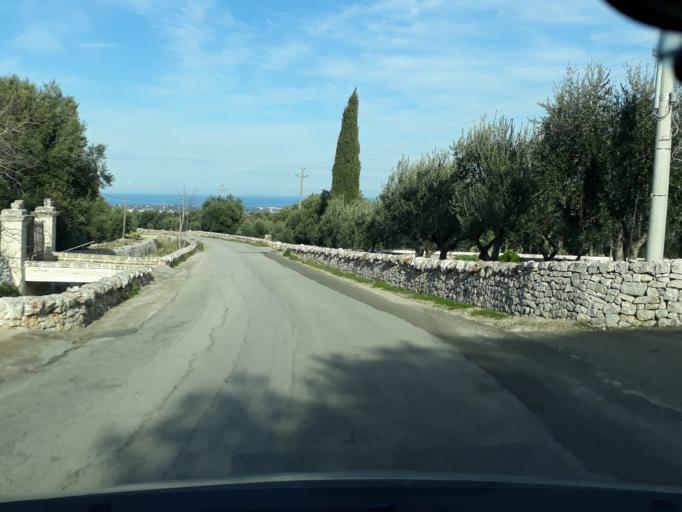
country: IT
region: Apulia
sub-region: Provincia di Brindisi
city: Lamie di Olimpie-Selva
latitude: 40.8089
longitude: 17.3546
